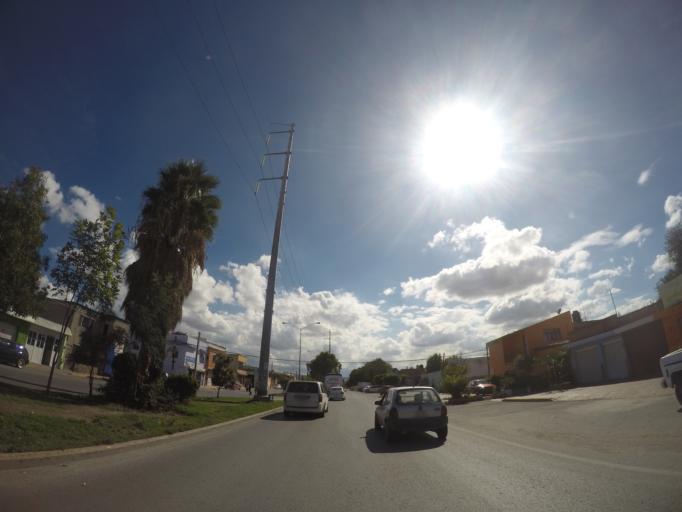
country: MX
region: San Luis Potosi
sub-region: San Luis Potosi
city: San Luis Potosi
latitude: 22.1654
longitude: -100.9601
